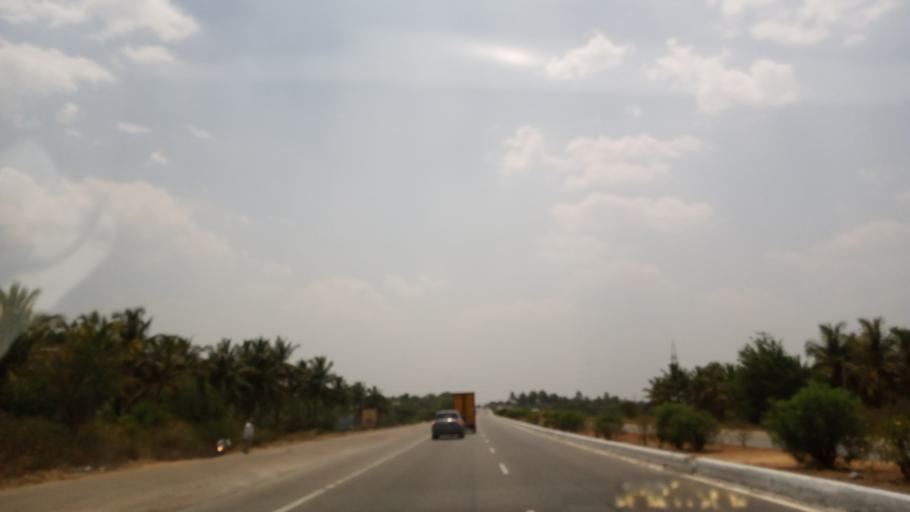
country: IN
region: Karnataka
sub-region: Tumkur
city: Kunigal
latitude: 12.9914
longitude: 76.8880
